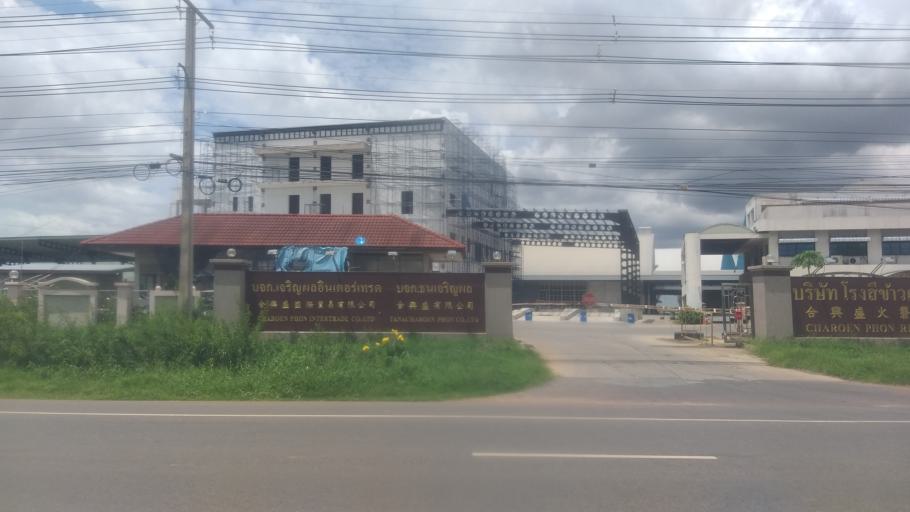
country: TH
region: Nakhon Ratchasima
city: Non Thai
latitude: 15.0878
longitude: 102.1112
